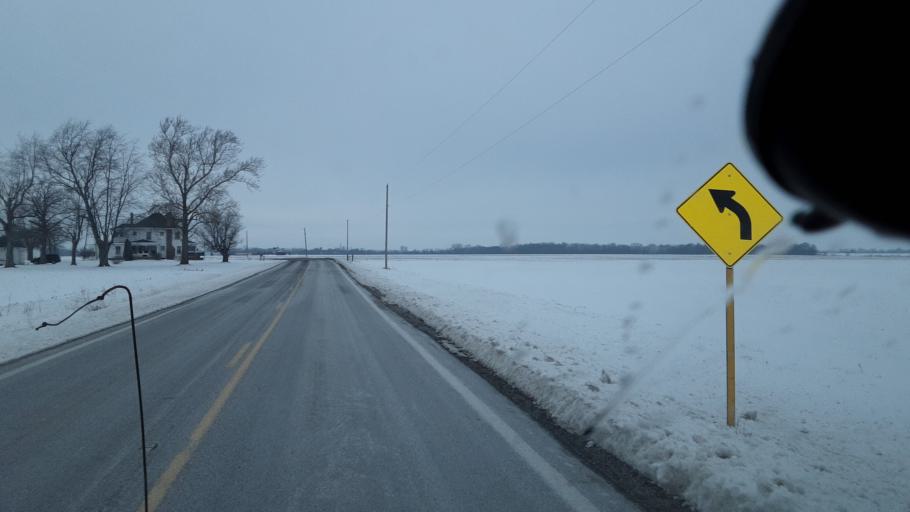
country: US
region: Ohio
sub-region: Champaign County
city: Mechanicsburg
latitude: 40.1191
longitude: -83.4357
